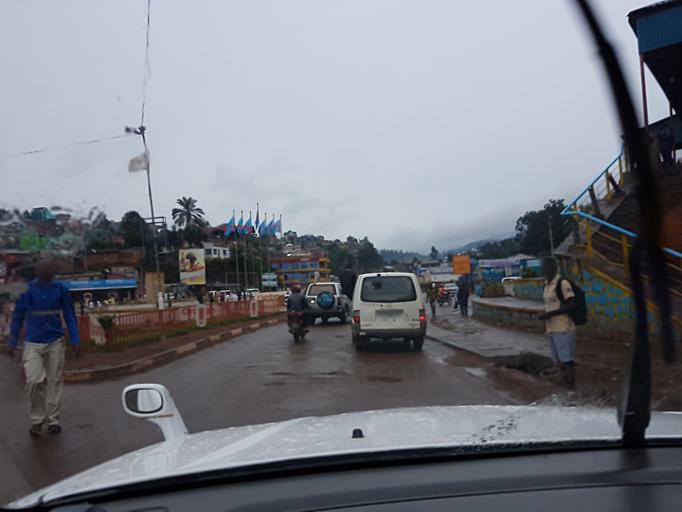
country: CD
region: South Kivu
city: Bukavu
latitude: -2.4999
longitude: 28.8514
